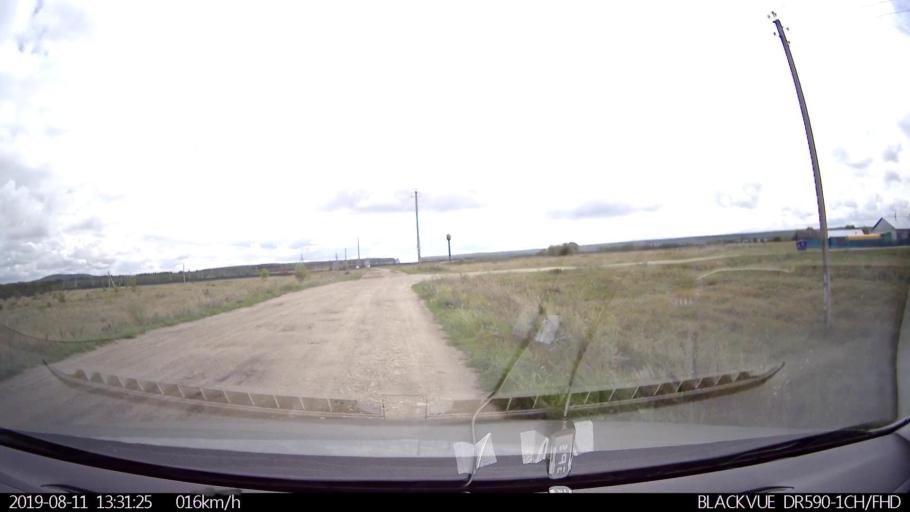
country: RU
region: Ulyanovsk
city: Ignatovka
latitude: 53.8592
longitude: 47.6001
